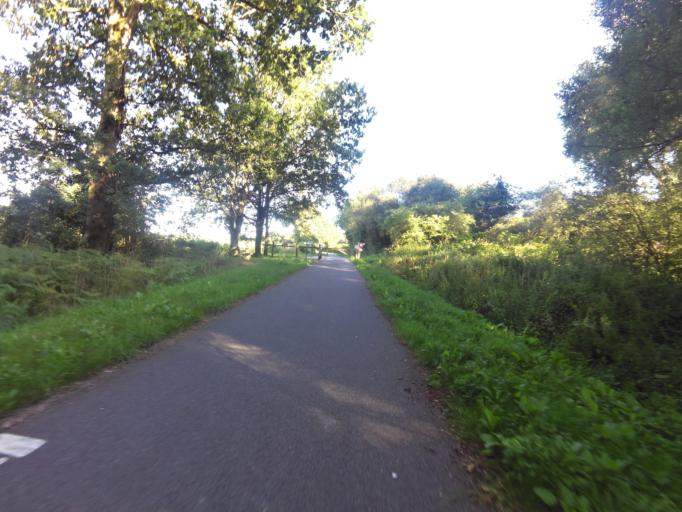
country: FR
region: Brittany
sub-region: Departement du Morbihan
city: Malestroit
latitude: 47.8198
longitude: -2.4179
